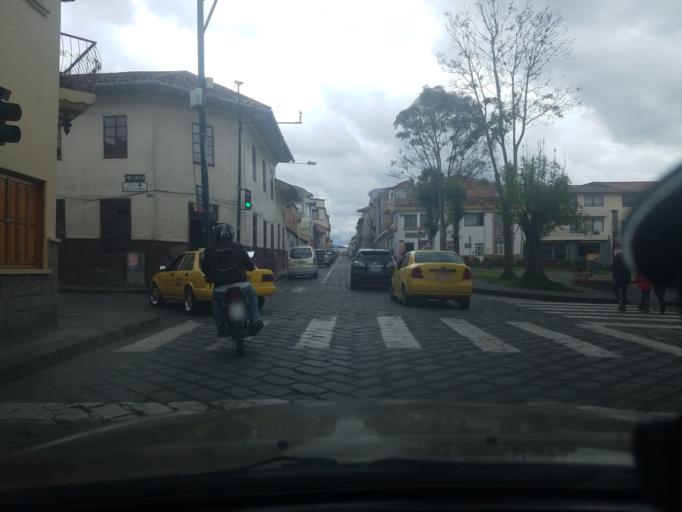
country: EC
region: Azuay
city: Cuenca
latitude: -2.9002
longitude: -79.0003
